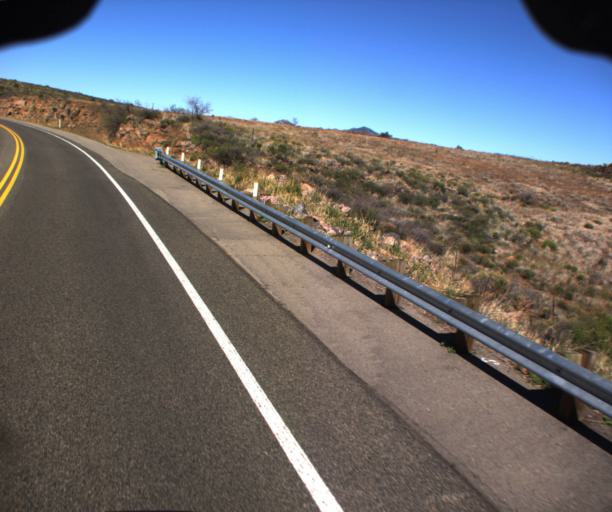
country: US
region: Arizona
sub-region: Yavapai County
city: Congress
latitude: 34.3282
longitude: -112.6951
